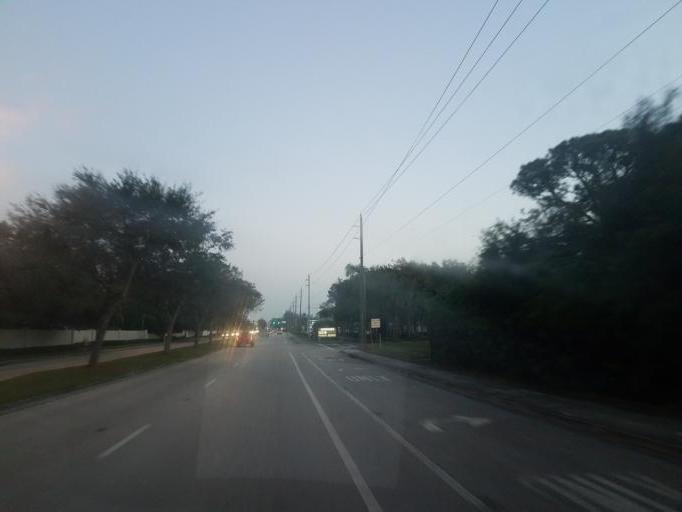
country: US
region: Florida
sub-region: Sarasota County
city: Lake Sarasota
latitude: 27.3090
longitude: -82.4514
